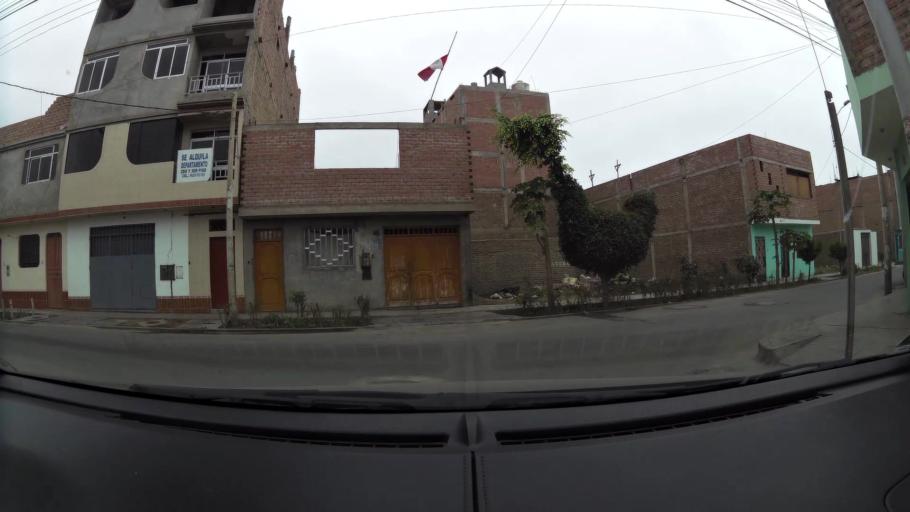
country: PE
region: Lima
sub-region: Barranca
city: Barranca
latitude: -10.7541
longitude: -77.7545
